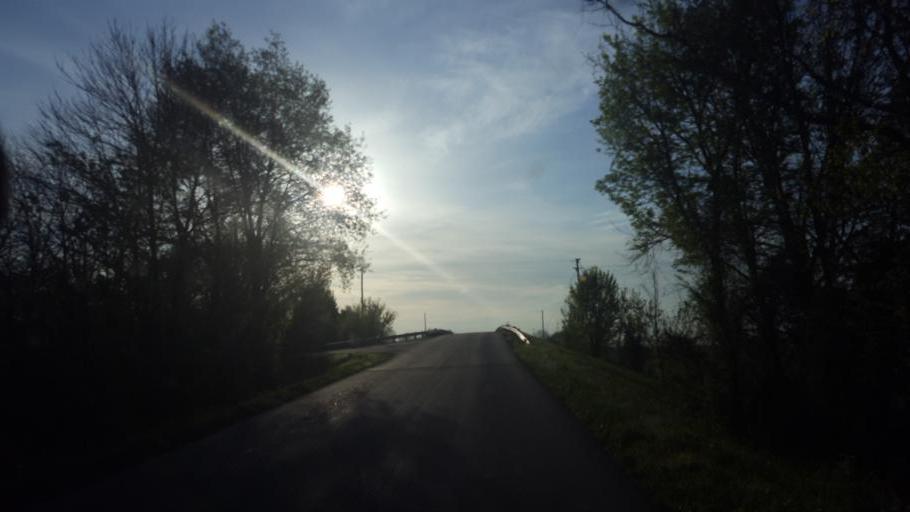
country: US
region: Kentucky
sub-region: Hart County
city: Munfordville
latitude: 37.2442
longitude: -85.9287
